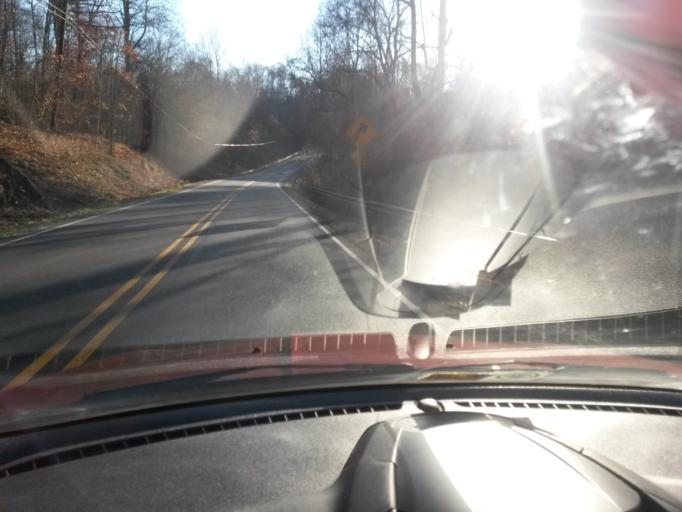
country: US
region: Virginia
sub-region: Amherst County
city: Amherst
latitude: 37.6118
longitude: -79.0802
